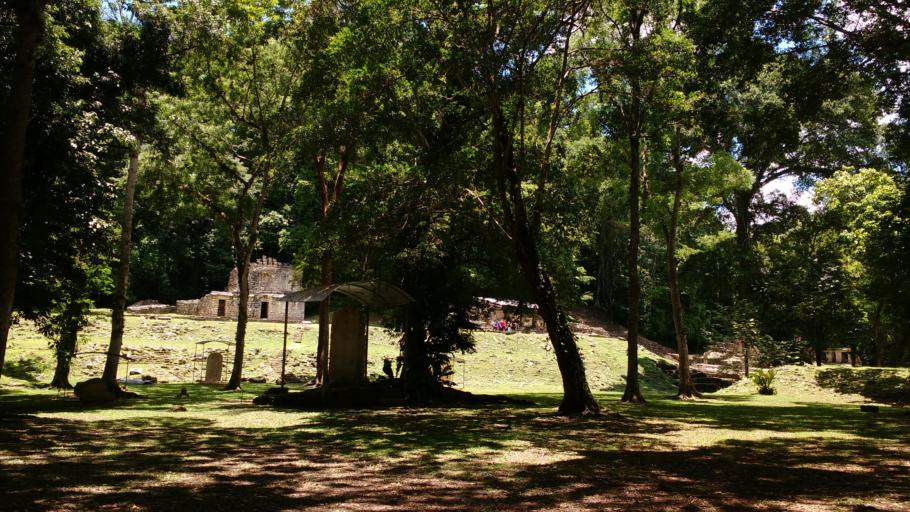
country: MX
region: Chiapas
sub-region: Ocosingo
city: Frontera Corozal
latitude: 16.8990
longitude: -90.9632
